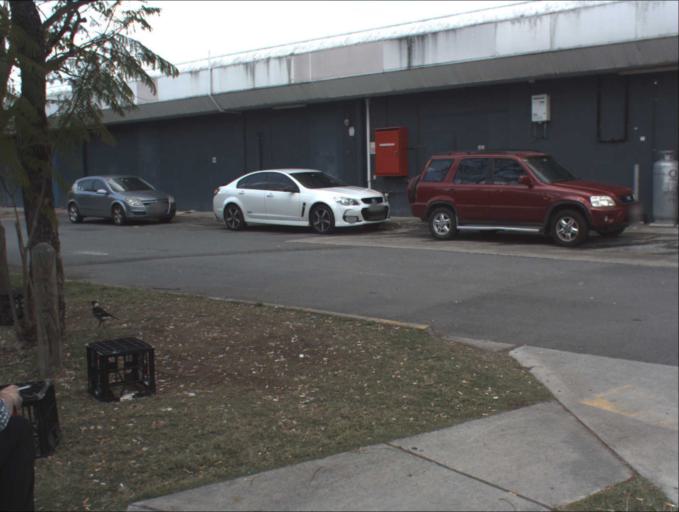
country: AU
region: Queensland
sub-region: Brisbane
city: Sunnybank Hills
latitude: -27.6592
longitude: 153.0396
